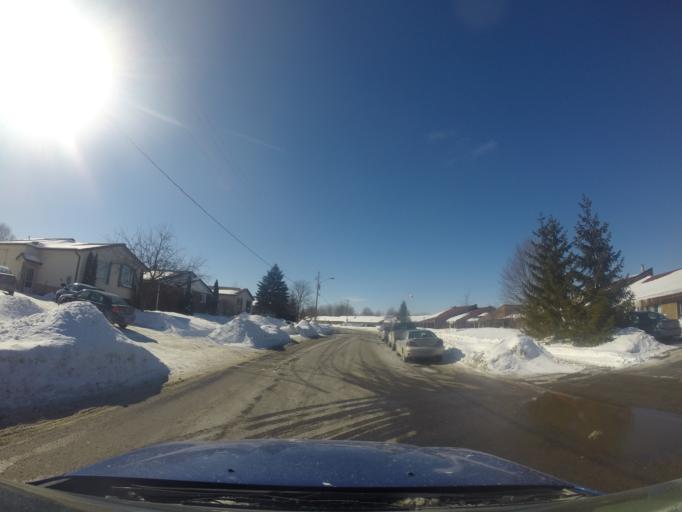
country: CA
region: Ontario
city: Omemee
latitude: 44.3428
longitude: -78.7489
